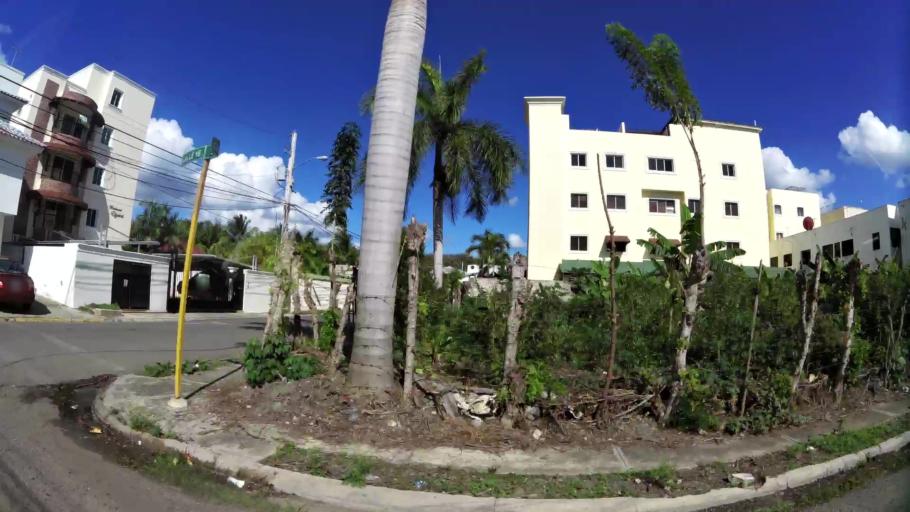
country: DO
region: Santiago
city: Santiago de los Caballeros
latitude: 19.4497
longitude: -70.6696
